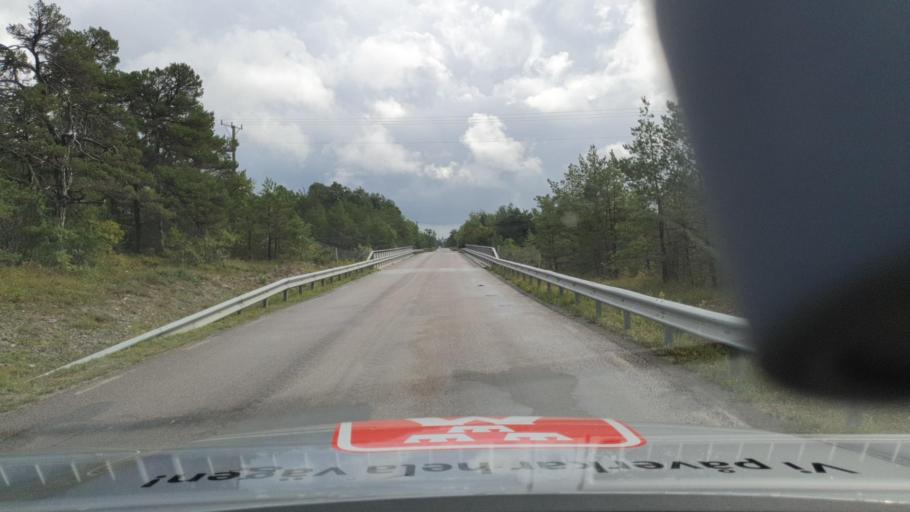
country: SE
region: Gotland
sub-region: Gotland
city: Slite
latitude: 57.7232
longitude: 18.7505
